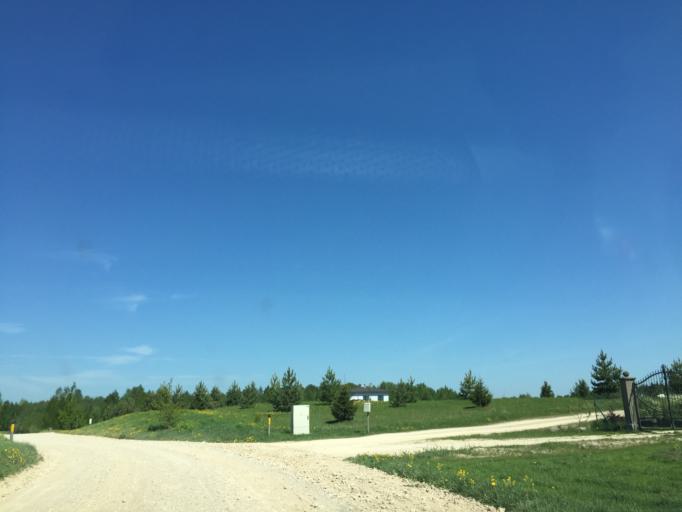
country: LV
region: Ikskile
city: Ikskile
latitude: 56.8679
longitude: 24.5026
